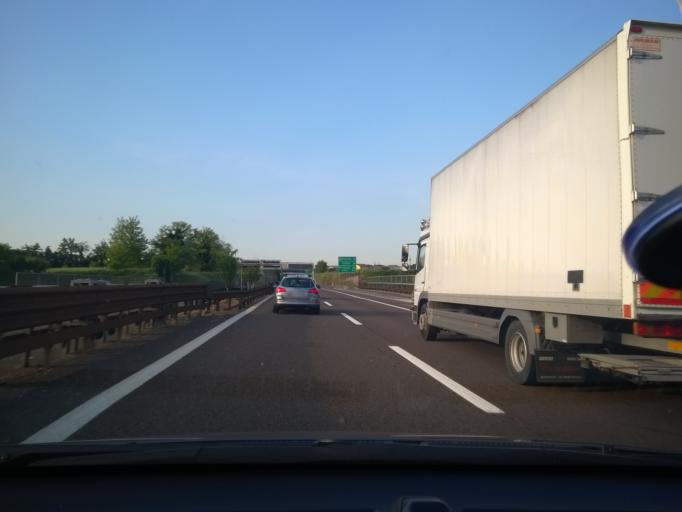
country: IT
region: Veneto
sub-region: Provincia di Verona
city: Dossobuono
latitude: 45.4008
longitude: 10.9109
